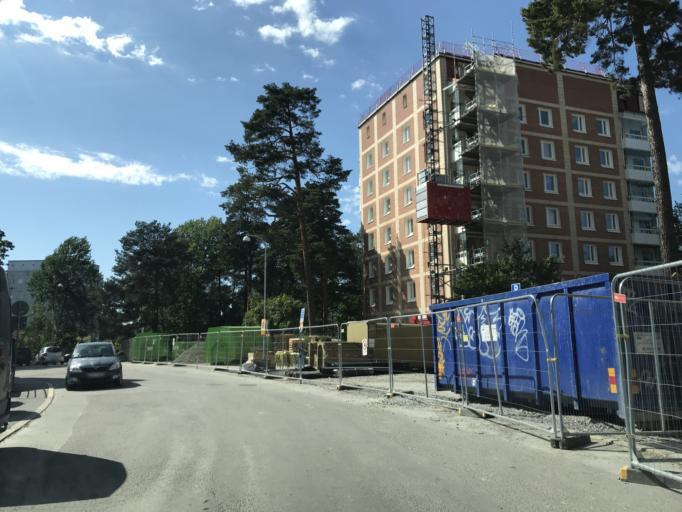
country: SE
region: Stockholm
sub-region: Solna Kommun
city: Solna
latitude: 59.3782
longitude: 18.0047
